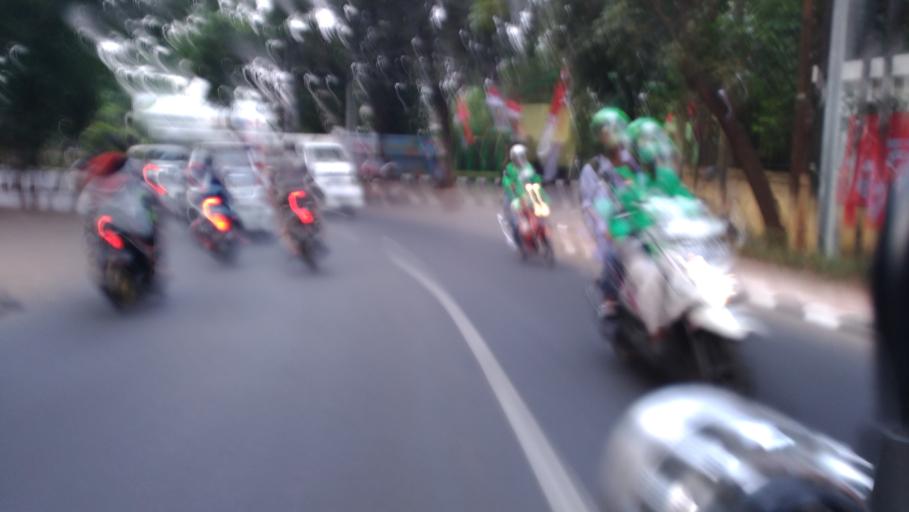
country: ID
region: West Java
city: Cileungsir
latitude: -6.3569
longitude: 106.8902
